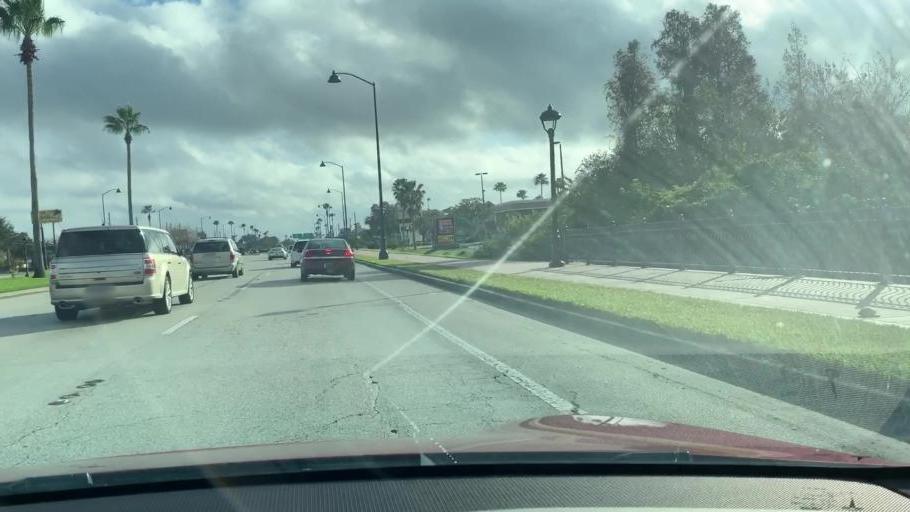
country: US
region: Florida
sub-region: Osceola County
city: Celebration
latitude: 28.3328
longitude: -81.4871
